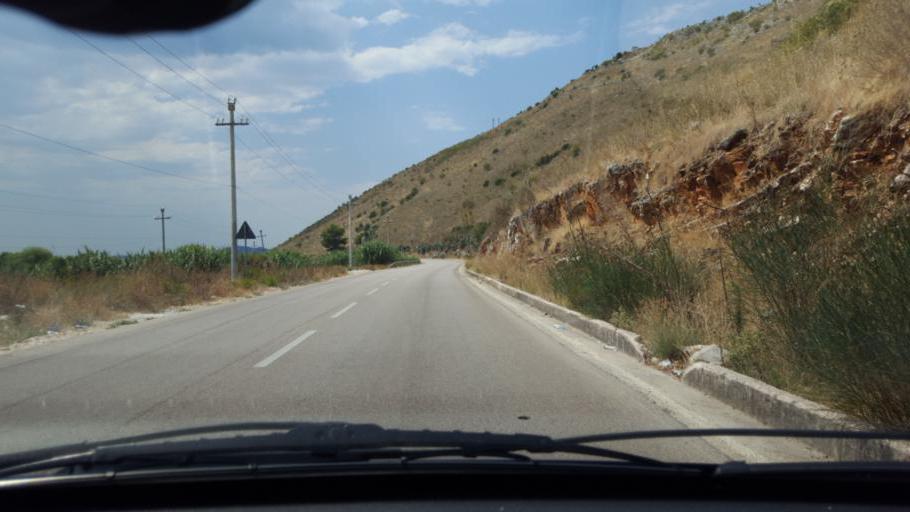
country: AL
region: Vlore
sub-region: Rrethi i Sarandes
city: Sarande
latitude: 39.8345
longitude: 20.0233
